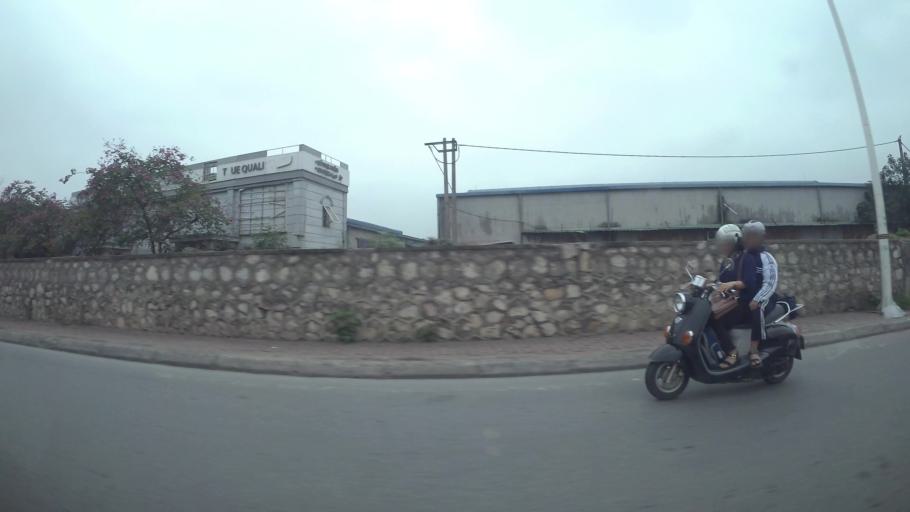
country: VN
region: Ha Noi
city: Hai BaTrung
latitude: 21.0033
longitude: 105.8718
